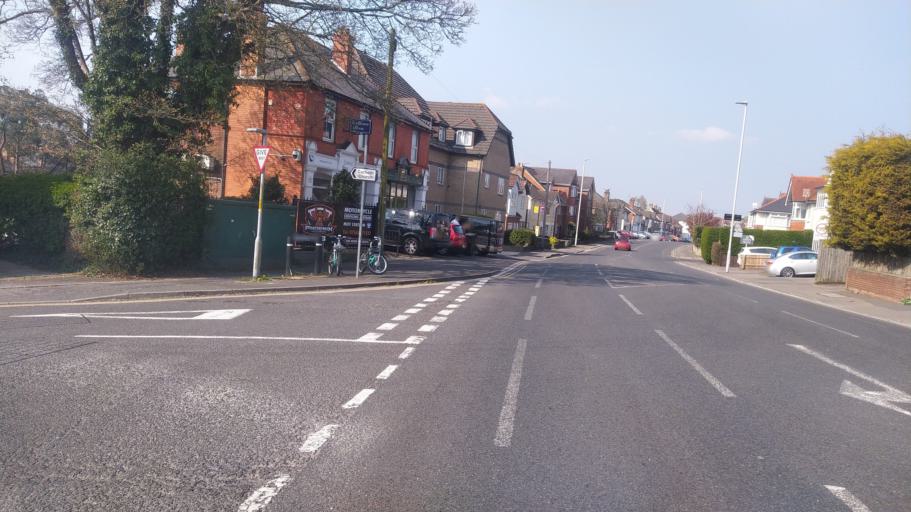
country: GB
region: England
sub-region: Dorset
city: Parkstone
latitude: 50.7248
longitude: -1.9286
